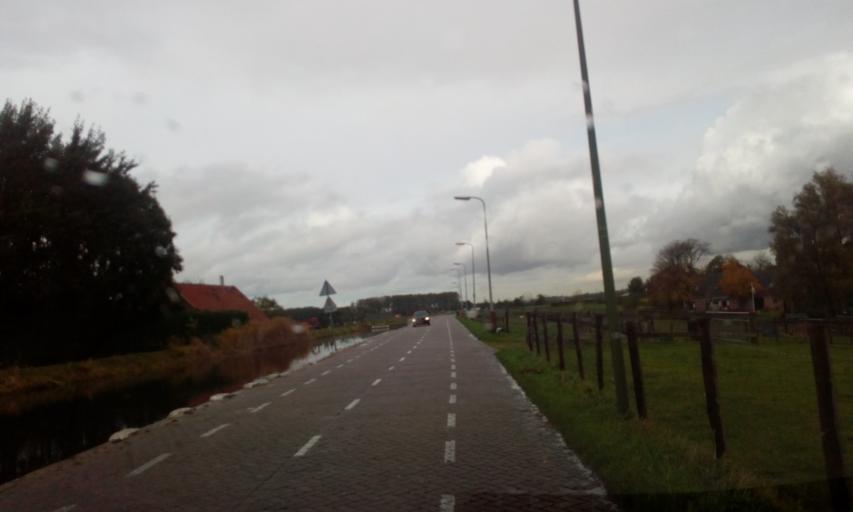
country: NL
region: South Holland
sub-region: Gemeente Voorschoten
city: Voorschoten
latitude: 52.0865
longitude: 4.4329
